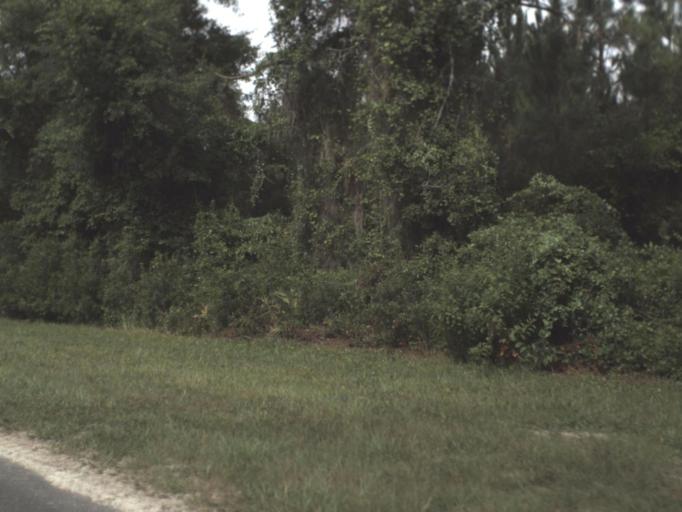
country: US
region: Florida
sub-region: Columbia County
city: Five Points
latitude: 30.3517
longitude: -82.6188
